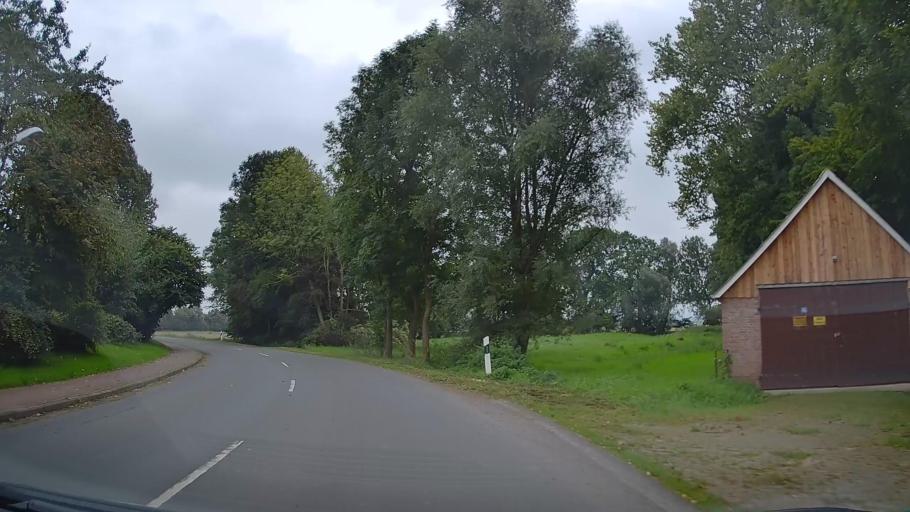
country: DE
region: Lower Saxony
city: Geversdorf
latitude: 53.8222
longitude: 9.0809
